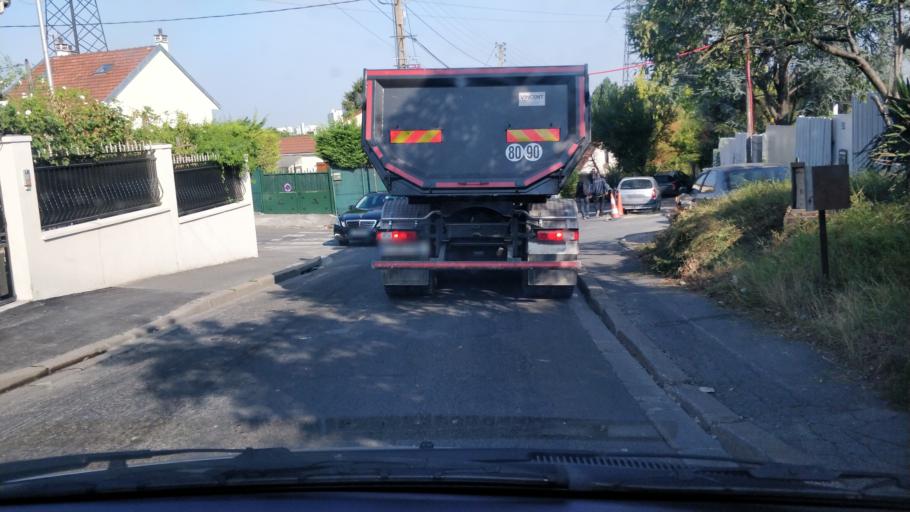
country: FR
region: Ile-de-France
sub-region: Departement de Seine-Saint-Denis
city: Villemomble
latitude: 48.8781
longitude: 2.4980
